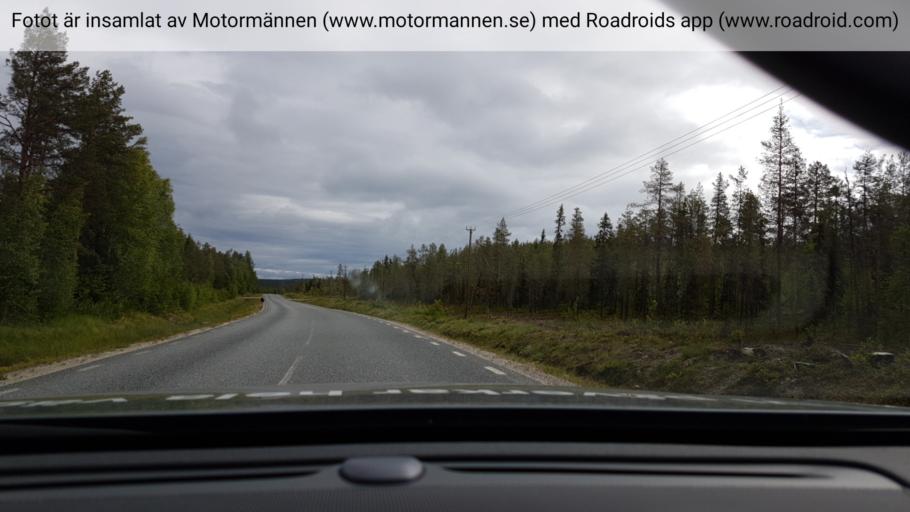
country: SE
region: Vaesterbotten
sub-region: Asele Kommun
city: Insjon
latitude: 64.2918
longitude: 17.6590
